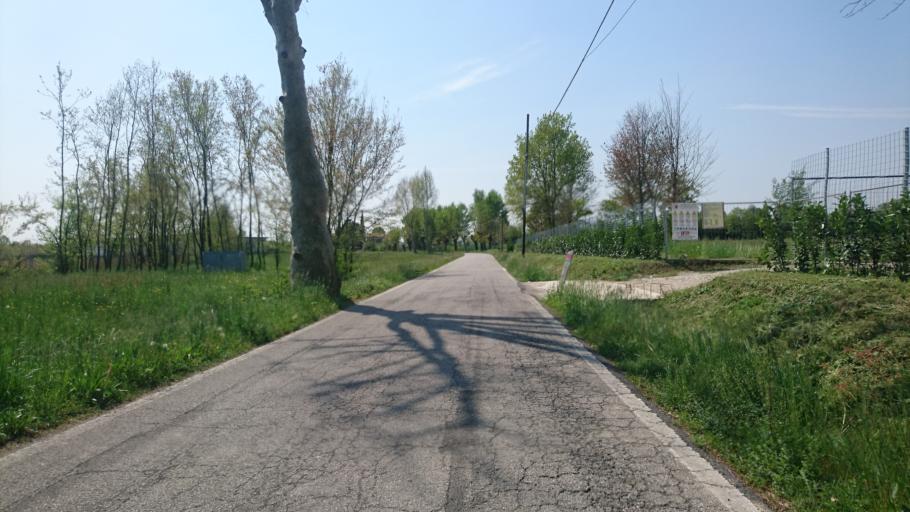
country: IT
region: Veneto
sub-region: Provincia di Padova
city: Rubano
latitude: 45.4129
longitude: 11.7969
